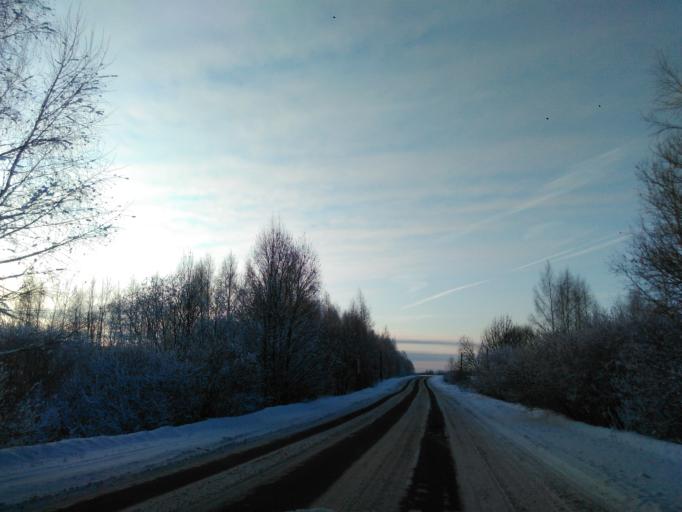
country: RU
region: Tverskaya
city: Zavidovo
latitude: 56.6236
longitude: 36.6151
